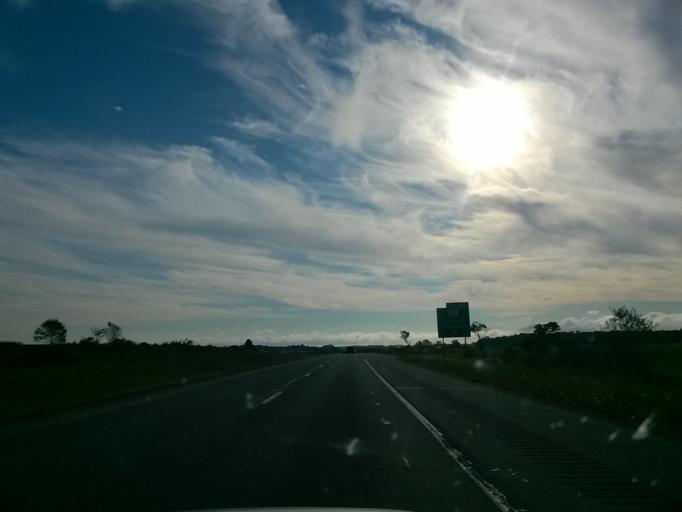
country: US
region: Indiana
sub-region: Spencer County
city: Dale
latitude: 38.1975
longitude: -87.0369
